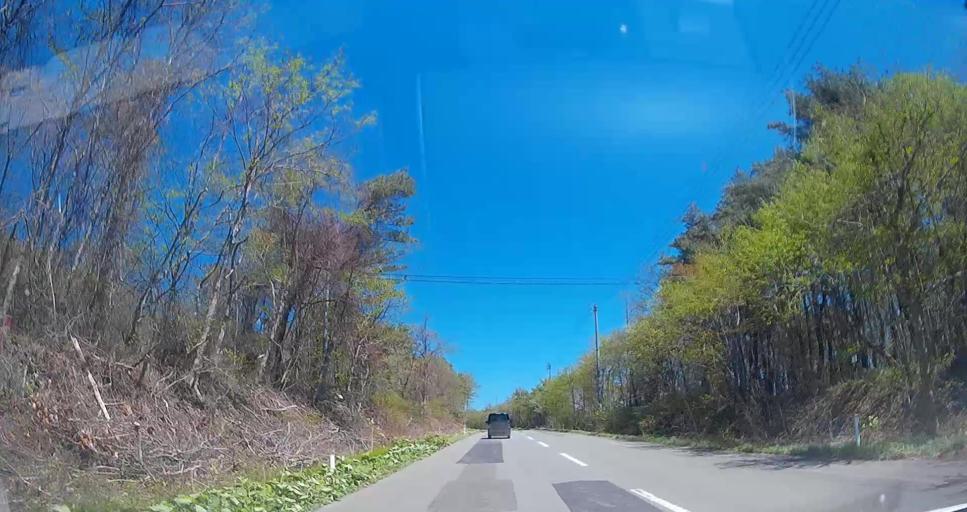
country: JP
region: Aomori
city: Mutsu
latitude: 41.2780
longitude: 141.3926
